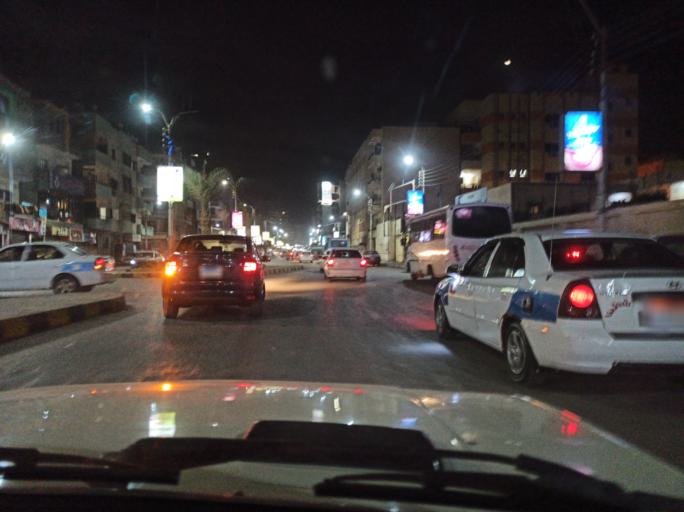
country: EG
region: Muhafazat Bani Suwayf
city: Bani Suwayf
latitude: 29.0709
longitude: 31.1009
